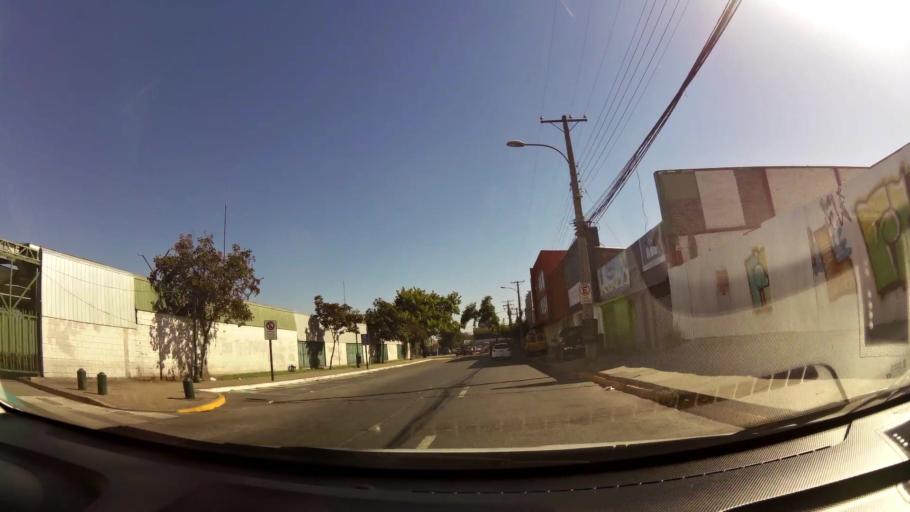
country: CL
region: O'Higgins
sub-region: Provincia de Cachapoal
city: Rancagua
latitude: -34.1660
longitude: -70.7505
